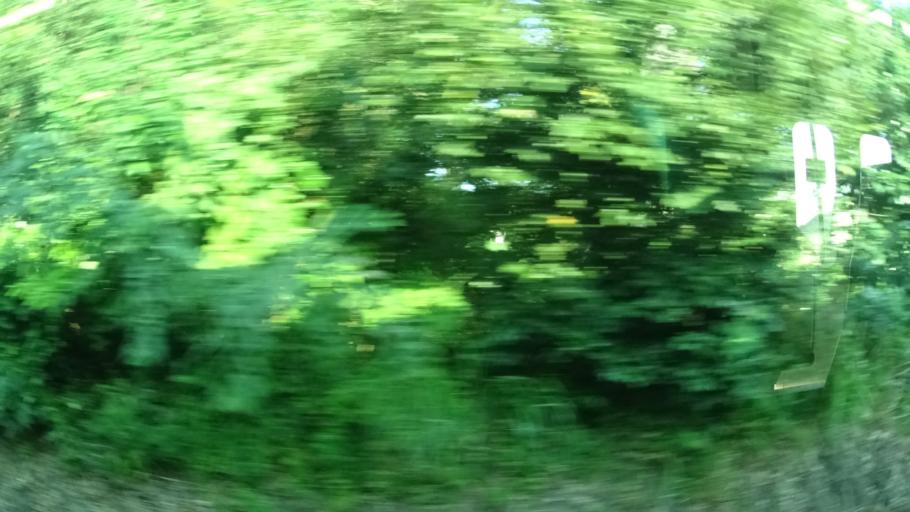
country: JP
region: Ibaraki
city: Kitaibaraki
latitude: 36.7549
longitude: 140.7299
